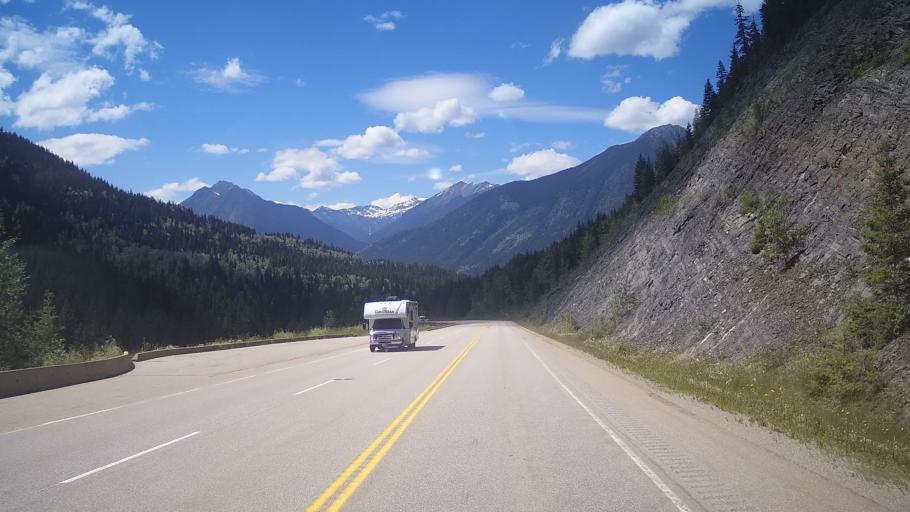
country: CA
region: Alberta
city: Grande Cache
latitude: 53.0289
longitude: -119.1738
